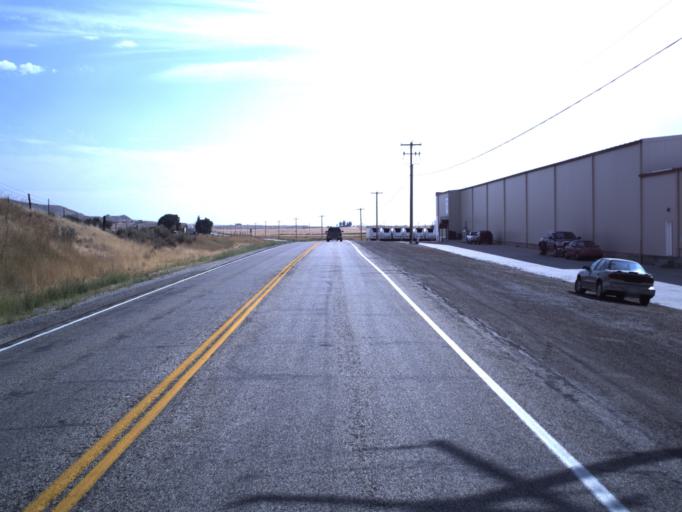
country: US
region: Utah
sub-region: Box Elder County
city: Garland
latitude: 41.7735
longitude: -112.0958
